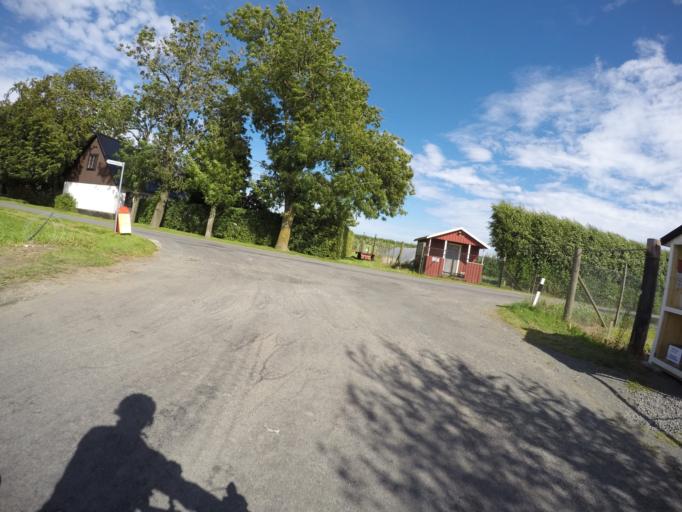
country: SE
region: Skane
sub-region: Simrishamns Kommun
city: Simrishamn
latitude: 55.4879
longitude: 14.1947
